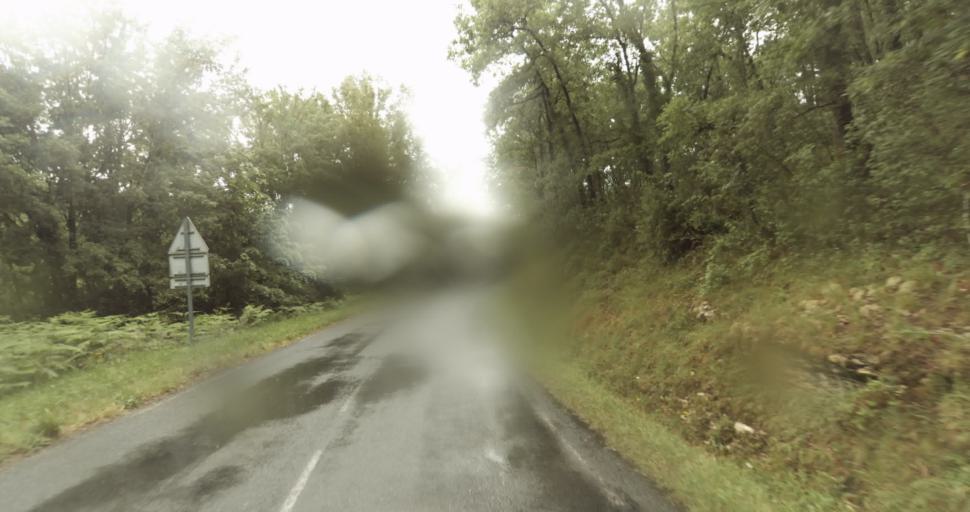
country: FR
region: Aquitaine
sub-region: Departement de la Dordogne
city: Le Bugue
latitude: 44.8313
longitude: 0.8984
